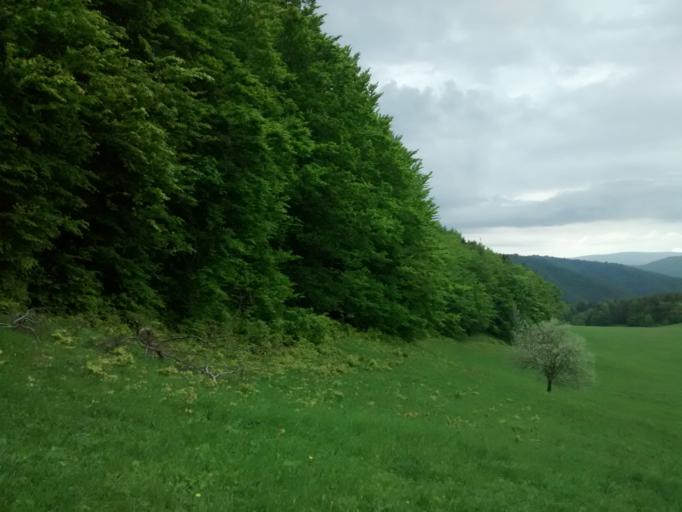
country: SK
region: Banskobystricky
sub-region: Okres Banska Bystrica
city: Banska Bystrica
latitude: 48.8703
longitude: 19.2184
